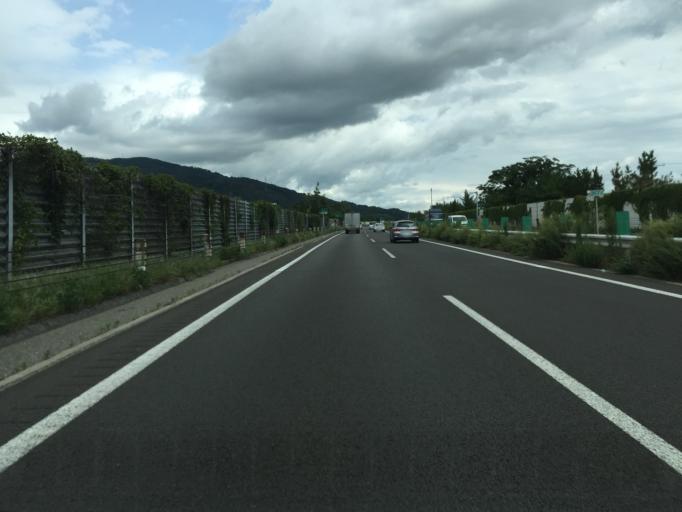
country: JP
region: Fukushima
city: Fukushima-shi
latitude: 37.8207
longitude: 140.4752
